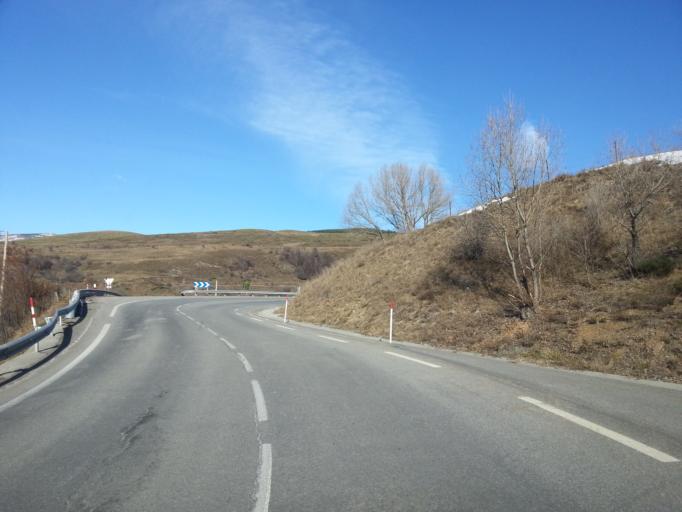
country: ES
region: Catalonia
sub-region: Provincia de Girona
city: Llivia
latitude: 42.4669
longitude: 2.0340
